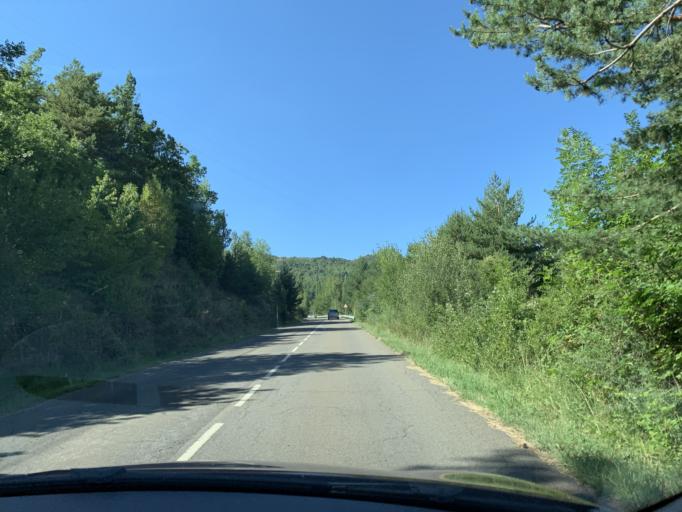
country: ES
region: Aragon
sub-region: Provincia de Huesca
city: Hoz de Jaca
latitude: 42.7009
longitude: -0.3203
